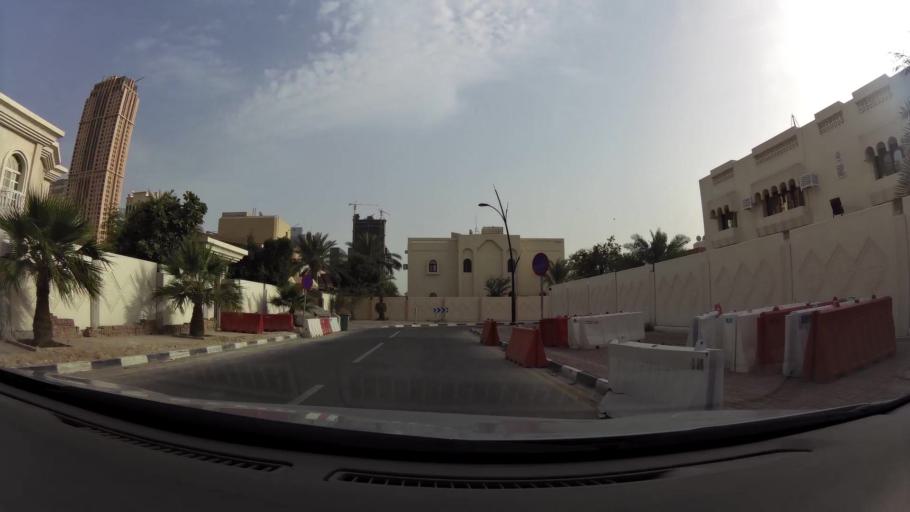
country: QA
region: Baladiyat ad Dawhah
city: Doha
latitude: 25.3277
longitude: 51.5197
